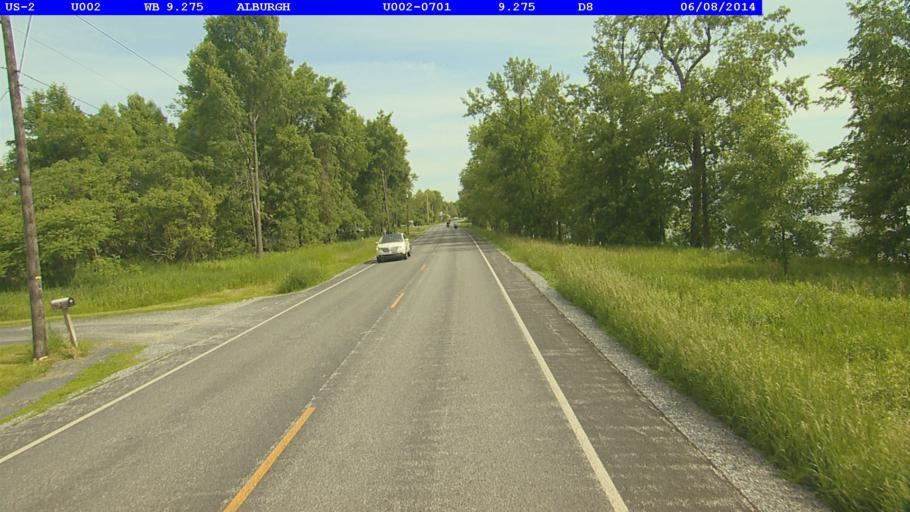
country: US
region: Vermont
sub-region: Grand Isle County
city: North Hero
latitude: 44.9172
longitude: -73.2763
